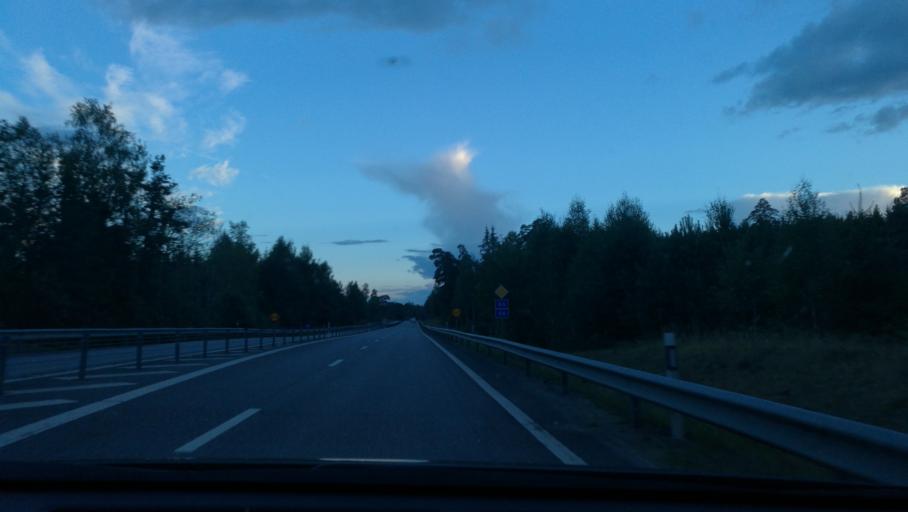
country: SE
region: Soedermanland
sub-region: Katrineholms Kommun
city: Katrineholm
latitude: 58.8518
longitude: 16.2064
